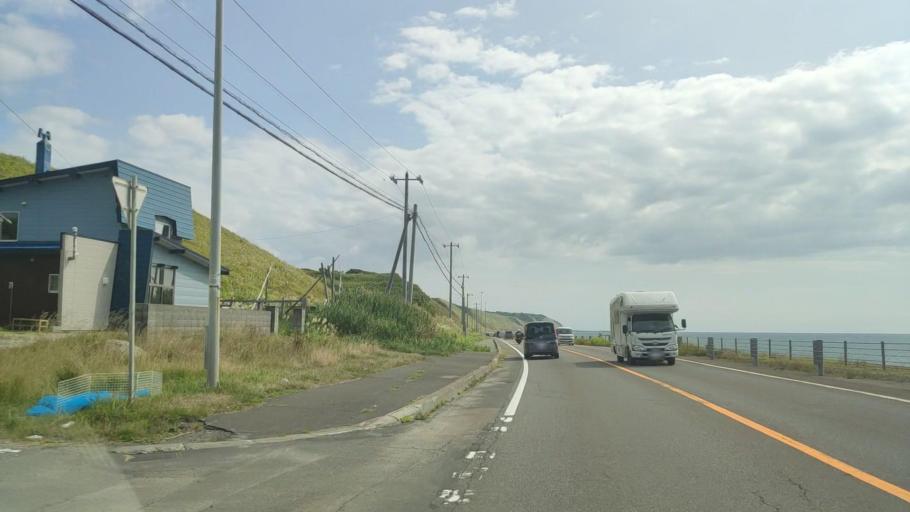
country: JP
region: Hokkaido
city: Rumoi
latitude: 44.2551
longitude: 141.6564
